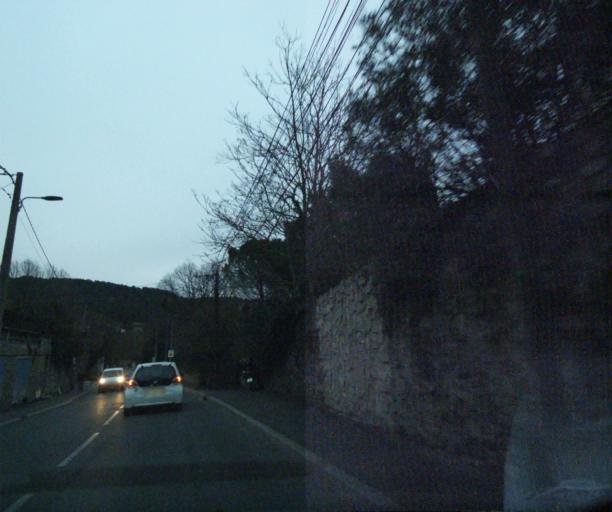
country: FR
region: Provence-Alpes-Cote d'Azur
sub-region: Departement des Bouches-du-Rhone
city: Aix-en-Provence
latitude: 43.5267
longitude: 5.4617
